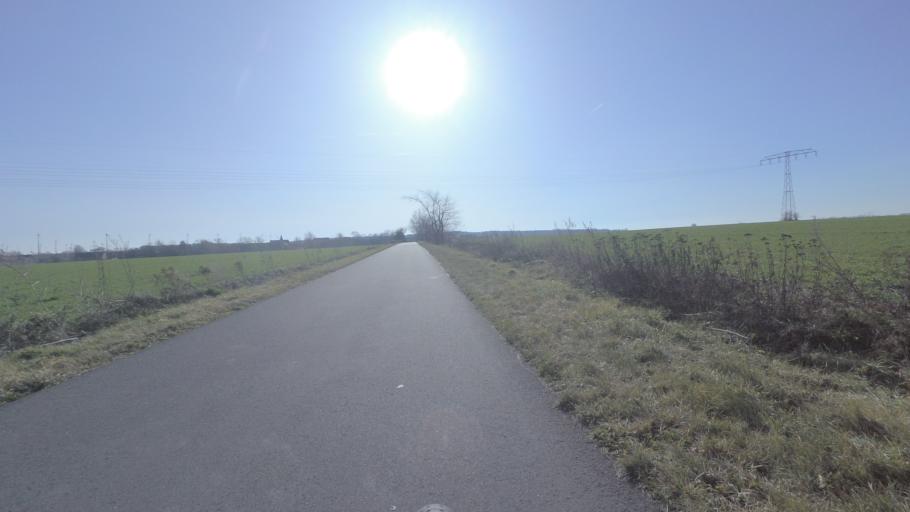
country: DE
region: Brandenburg
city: Luckenwalde
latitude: 52.0443
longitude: 13.1350
